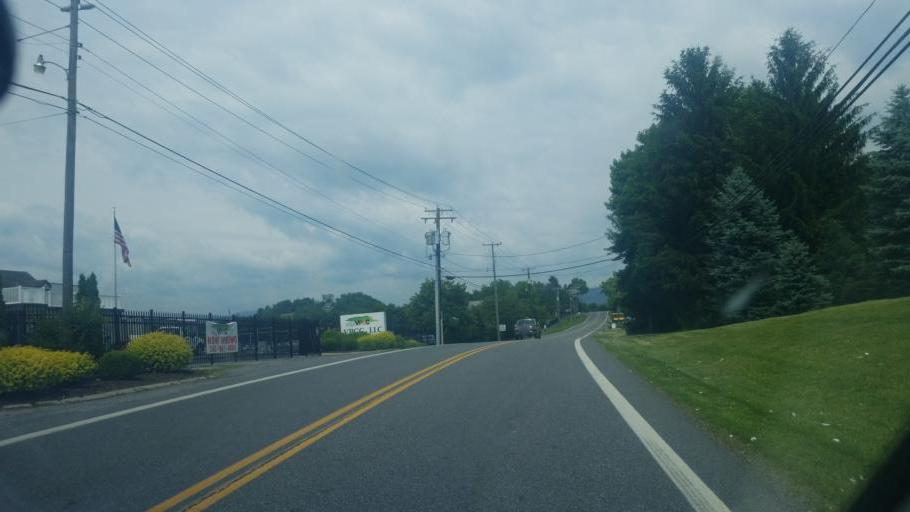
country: US
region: Virginia
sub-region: Rockingham County
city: Dayton
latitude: 38.4680
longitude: -78.9761
